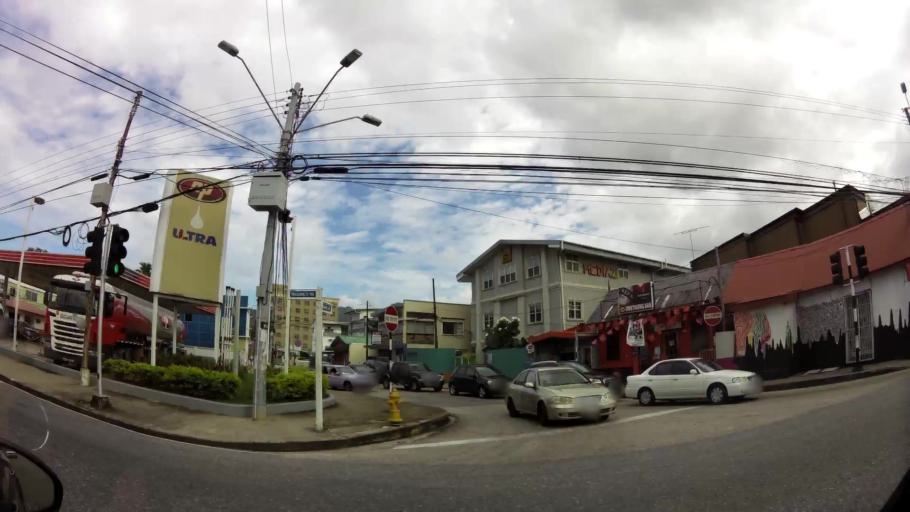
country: TT
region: City of Port of Spain
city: Port-of-Spain
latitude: 10.6625
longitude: -61.5195
